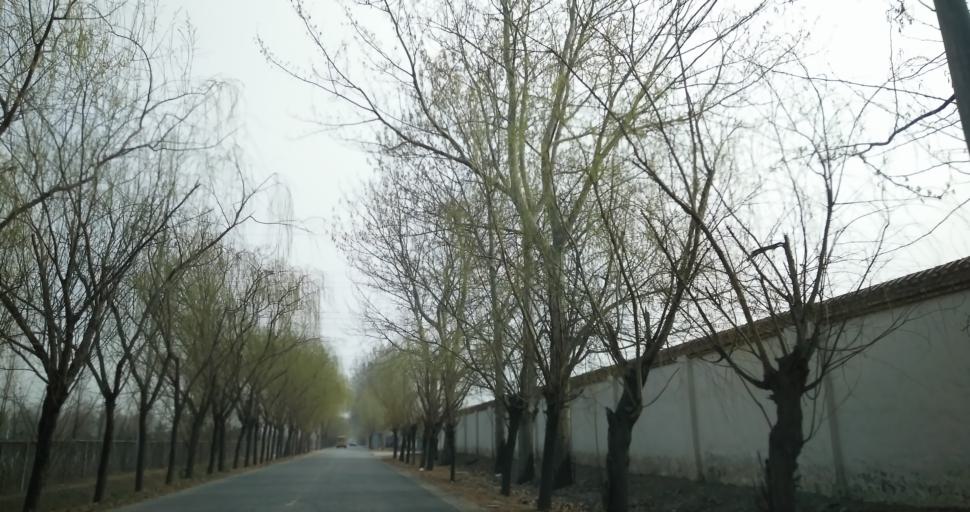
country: CN
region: Beijing
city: Qingyundian
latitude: 39.6984
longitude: 116.4970
